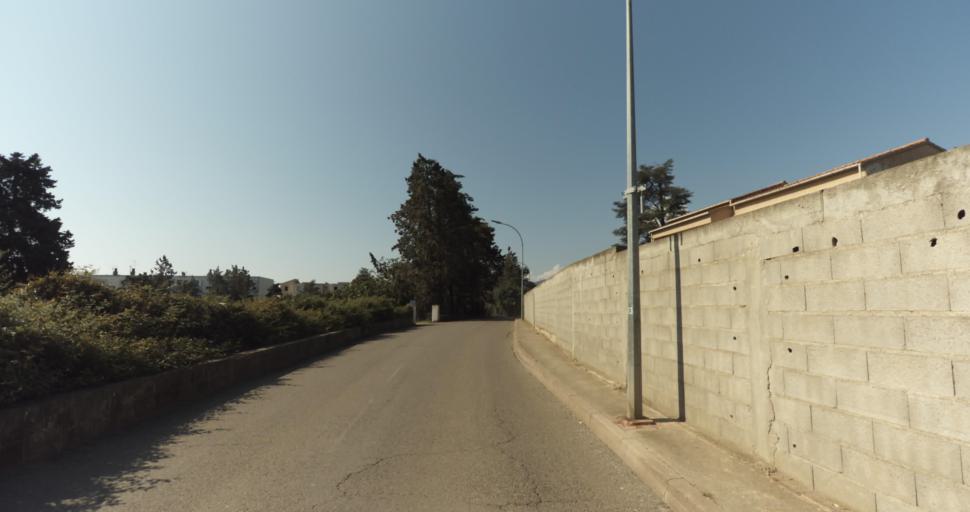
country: FR
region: Corsica
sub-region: Departement de la Haute-Corse
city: Biguglia
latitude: 42.6219
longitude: 9.4354
